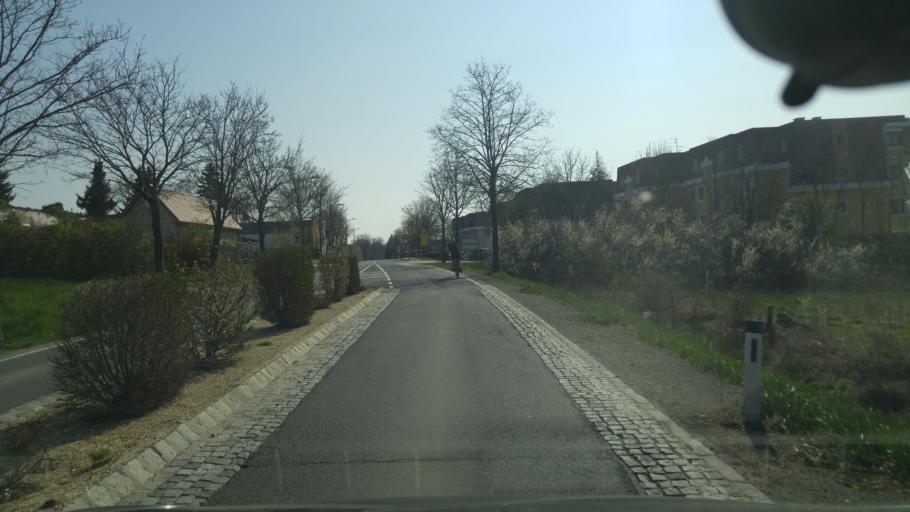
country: AT
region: Lower Austria
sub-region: Politischer Bezirk Wien-Umgebung
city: Moosbrunn
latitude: 48.0176
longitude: 16.4502
